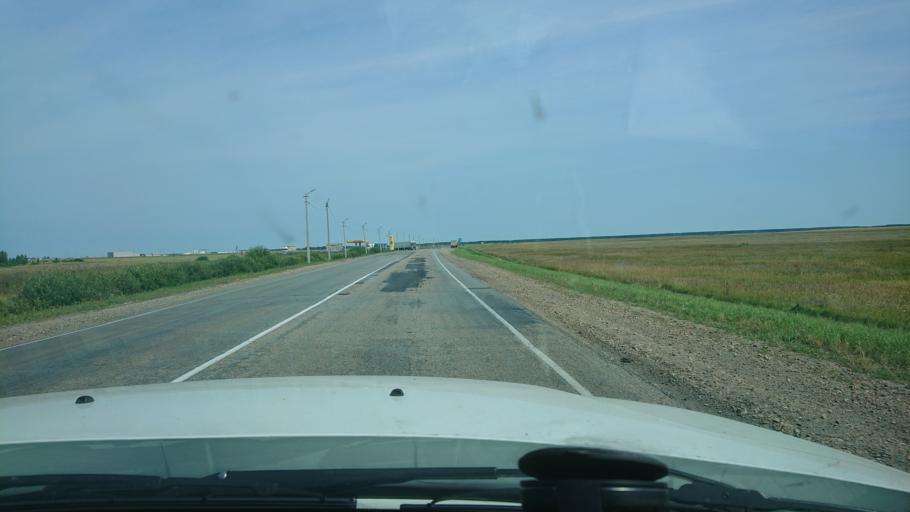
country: RU
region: Kurgan
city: Petukhovo
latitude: 55.5343
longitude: 67.8906
